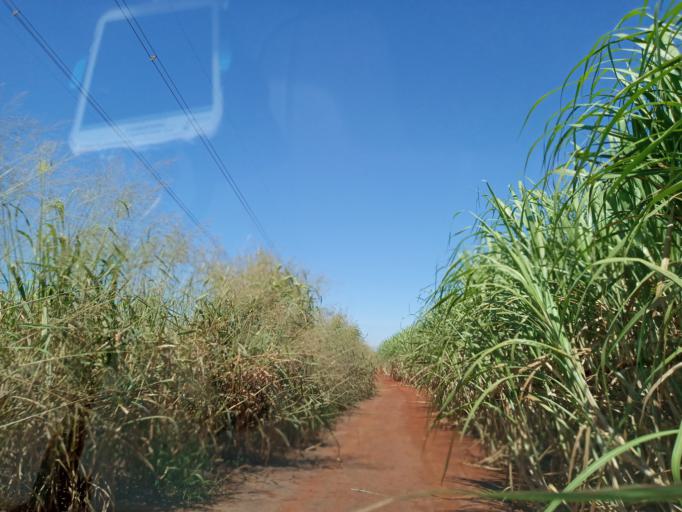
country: BR
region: Goias
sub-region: Itumbiara
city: Itumbiara
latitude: -18.4418
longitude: -49.1375
